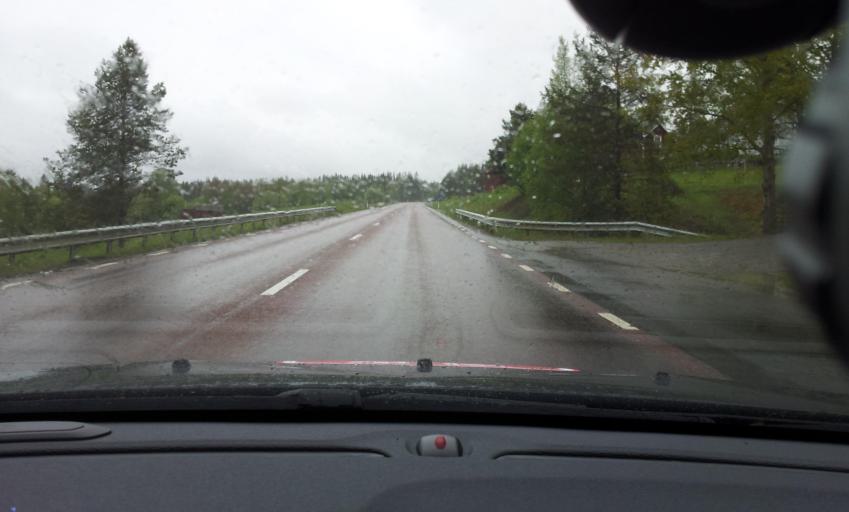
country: SE
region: Jaemtland
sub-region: Bergs Kommun
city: Hoverberg
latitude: 62.8981
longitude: 14.5232
